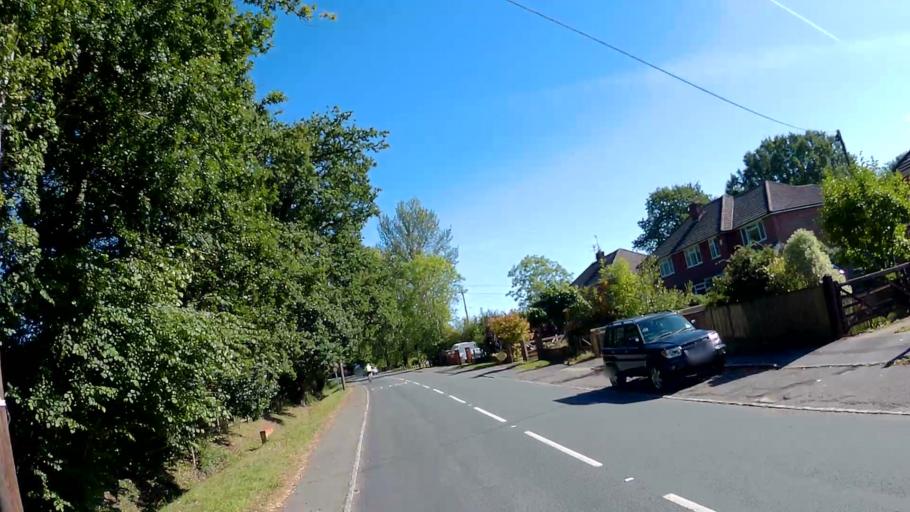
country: GB
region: England
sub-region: West Berkshire
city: Stratfield Mortimer
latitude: 51.3729
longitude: -1.0004
